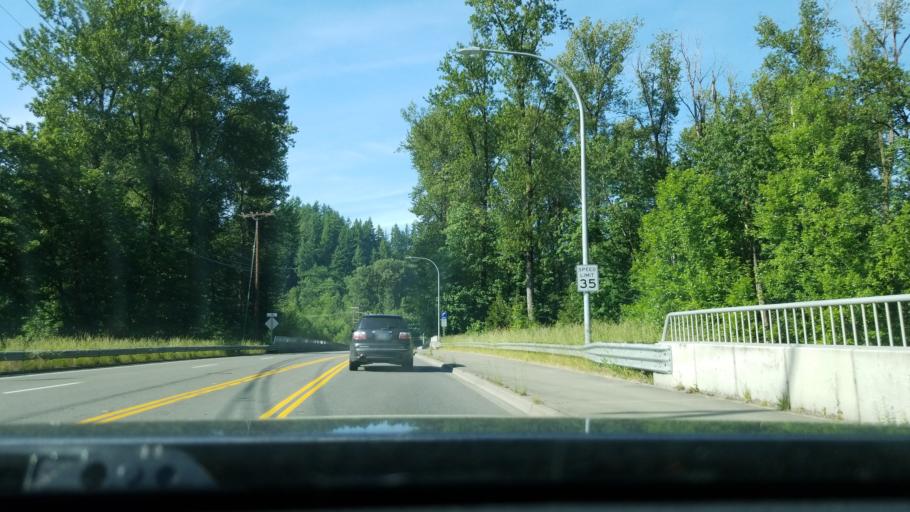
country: US
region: Washington
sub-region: King County
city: Fairwood
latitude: 47.4661
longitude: -122.1372
